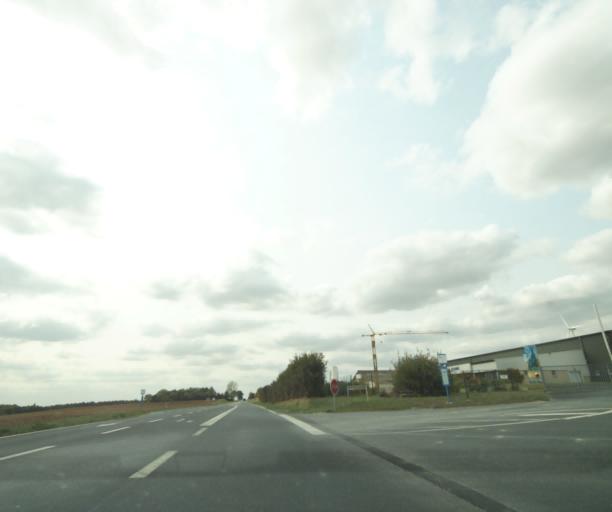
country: FR
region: Centre
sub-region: Departement de l'Indre
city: Buzancais
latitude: 46.9050
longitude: 1.3546
